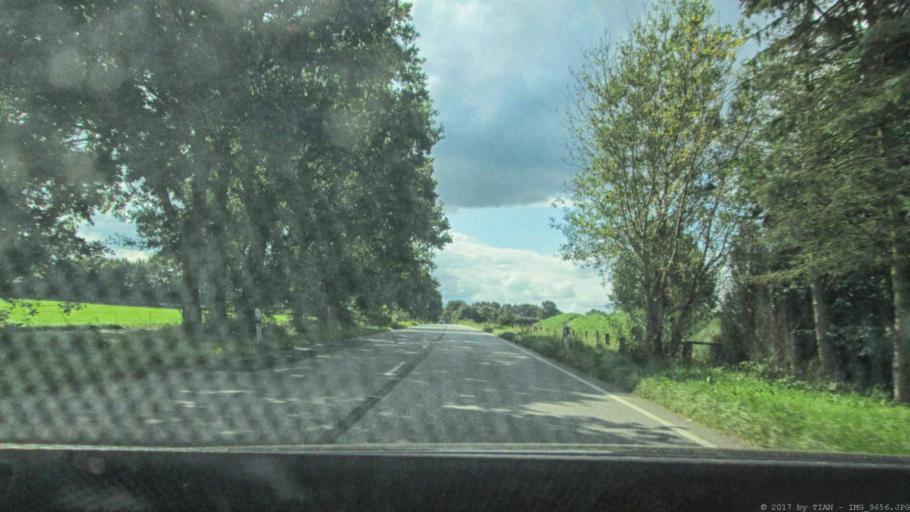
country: DE
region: Schleswig-Holstein
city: Kayhude
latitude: 53.7830
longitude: 10.1300
